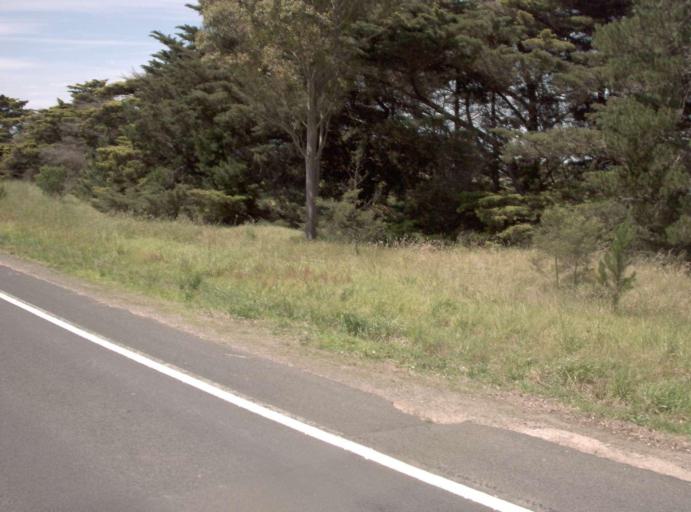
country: AU
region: Victoria
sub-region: Wellington
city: Sale
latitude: -38.0768
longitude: 147.0722
